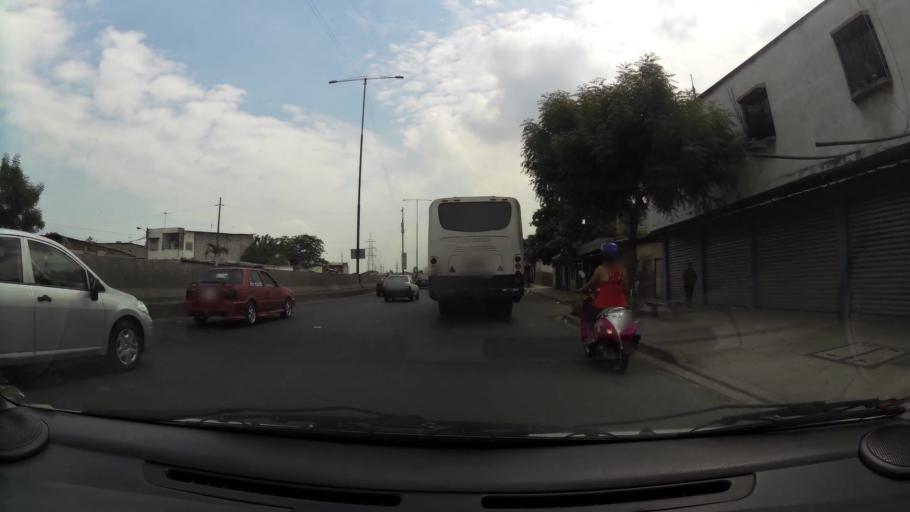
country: EC
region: Guayas
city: Guayaquil
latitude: -2.2388
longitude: -79.9103
